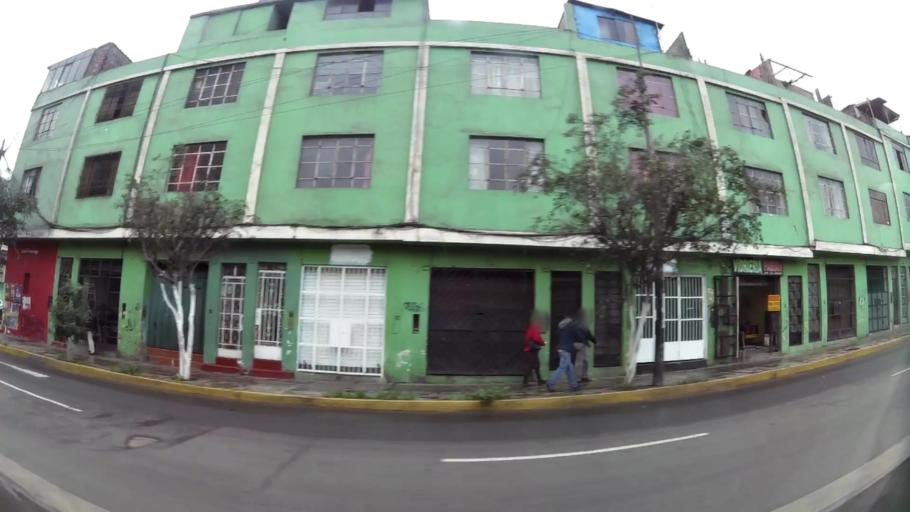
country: PE
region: Lima
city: Lima
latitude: -12.0697
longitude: -77.0259
